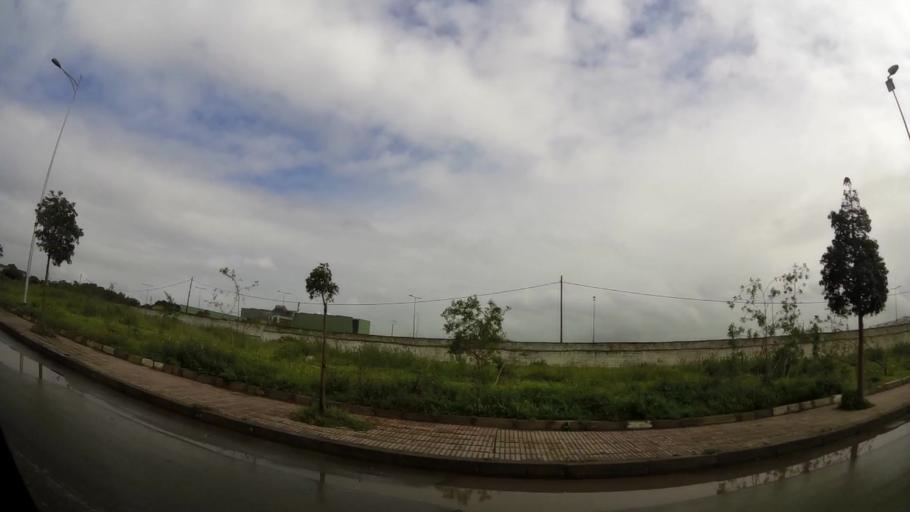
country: MA
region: Grand Casablanca
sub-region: Mohammedia
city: Mohammedia
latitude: 33.6368
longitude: -7.4445
